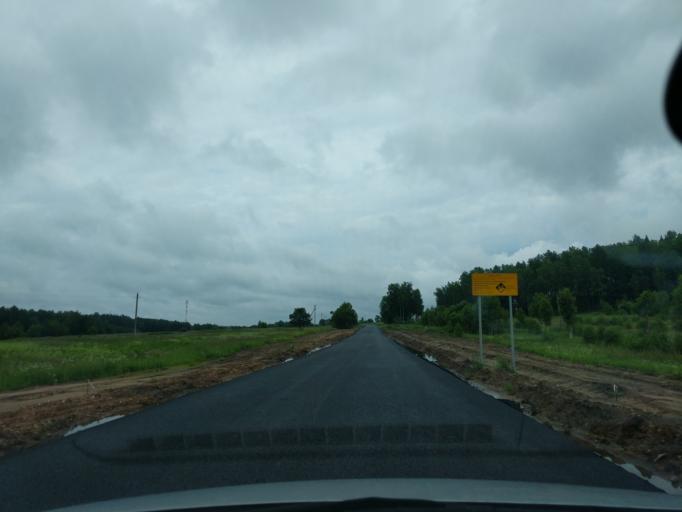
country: RU
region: Kaluga
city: Myatlevo
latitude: 54.8029
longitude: 35.7082
